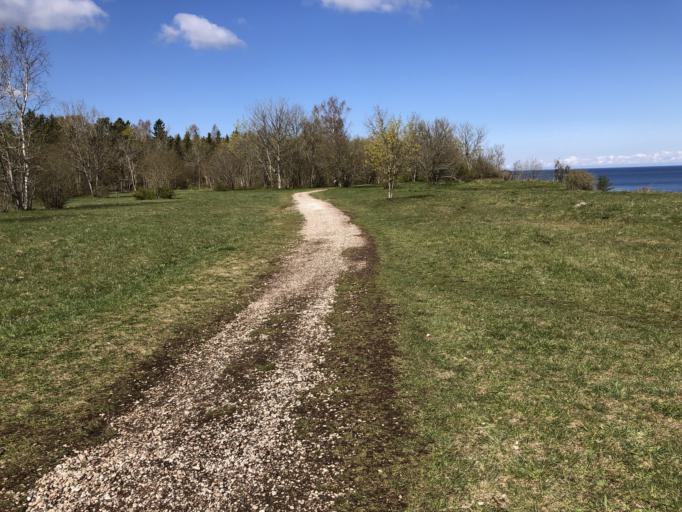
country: EE
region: Harju
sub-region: Harku vald
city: Tabasalu
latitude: 59.4386
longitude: 24.5376
